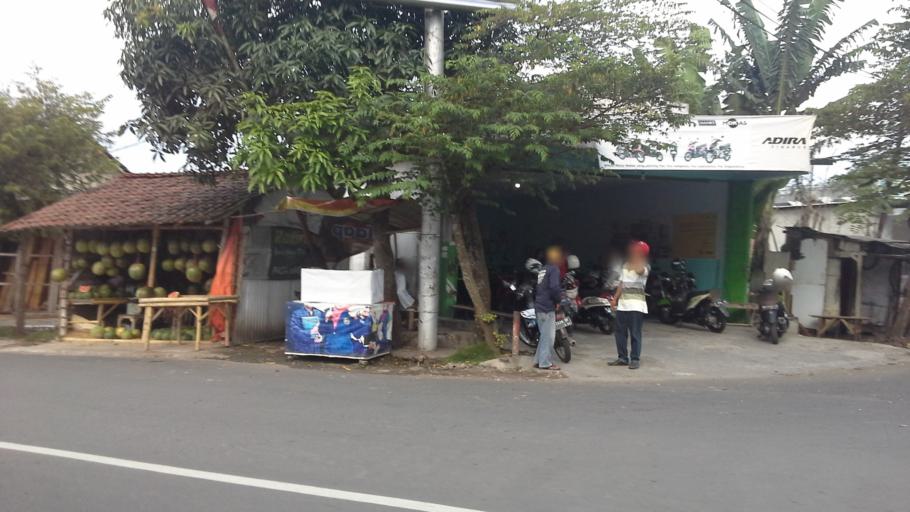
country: ID
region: East Java
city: Bondowoso
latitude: -7.9186
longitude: 113.8283
